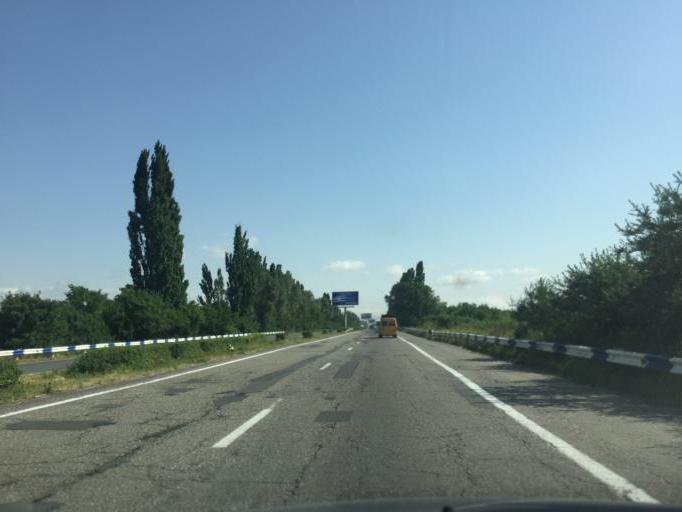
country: AM
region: Kotayk'i Marz
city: Solak
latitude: 40.4348
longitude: 44.7096
